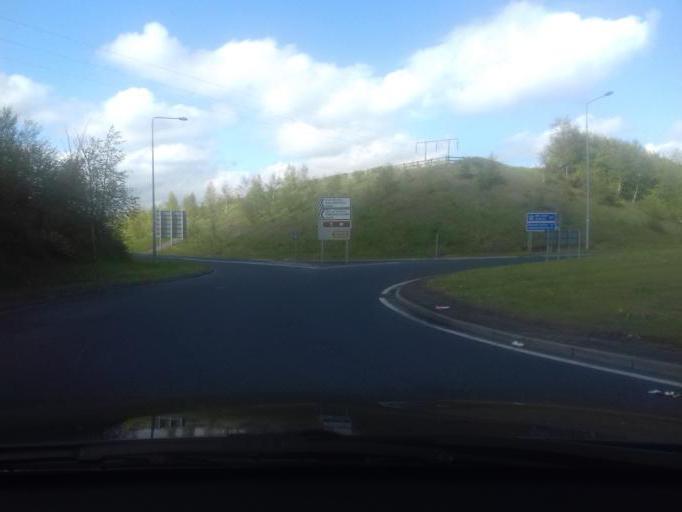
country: IE
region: Leinster
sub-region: Laois
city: Portlaoise
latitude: 53.0503
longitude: -7.2413
